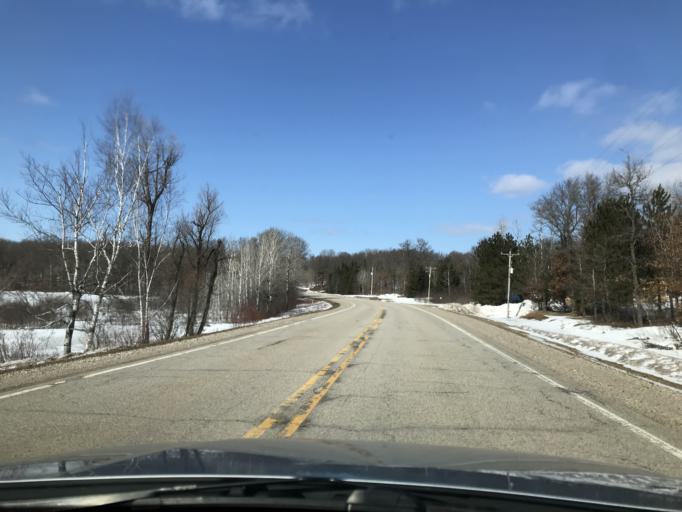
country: US
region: Wisconsin
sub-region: Marinette County
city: Niagara
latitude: 45.3355
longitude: -88.1009
